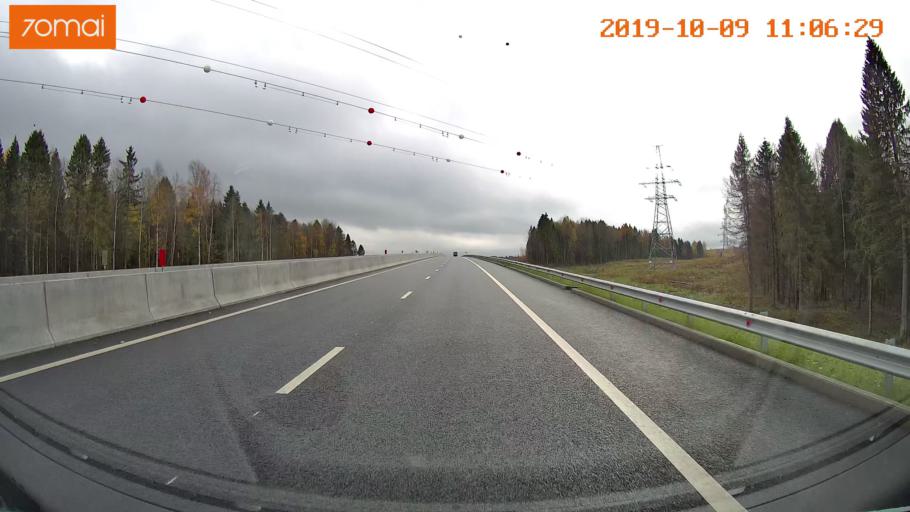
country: RU
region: Vologda
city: Vologda
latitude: 59.1859
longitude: 39.7609
